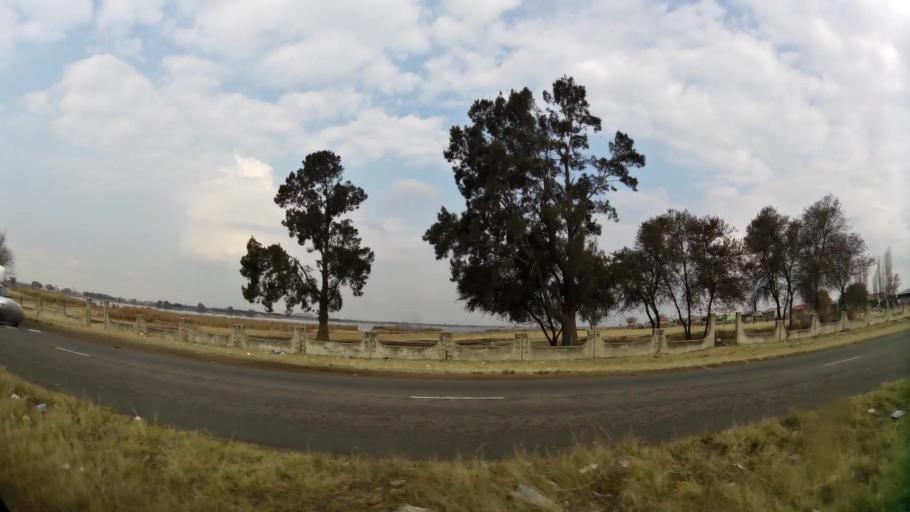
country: ZA
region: Gauteng
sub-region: Sedibeng District Municipality
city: Vereeniging
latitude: -26.6791
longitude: 27.8867
